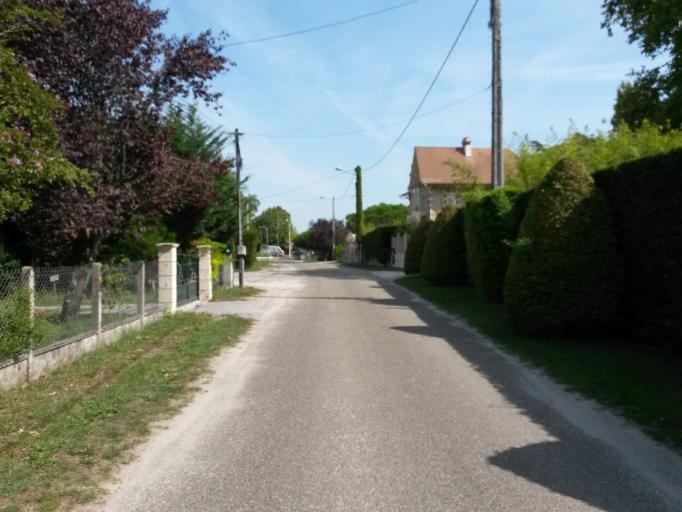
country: FR
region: Aquitaine
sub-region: Departement de la Gironde
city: Lanton
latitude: 44.7006
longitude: -1.0336
